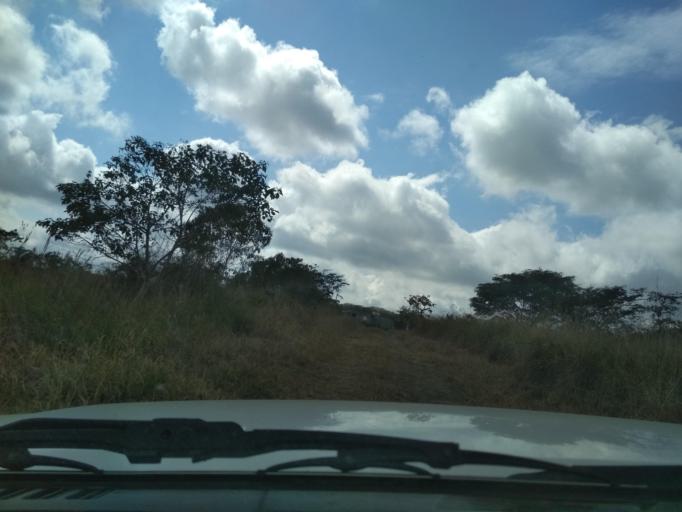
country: MX
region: Veracruz
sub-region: Emiliano Zapata
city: Dos Rios
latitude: 19.5035
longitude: -96.8225
